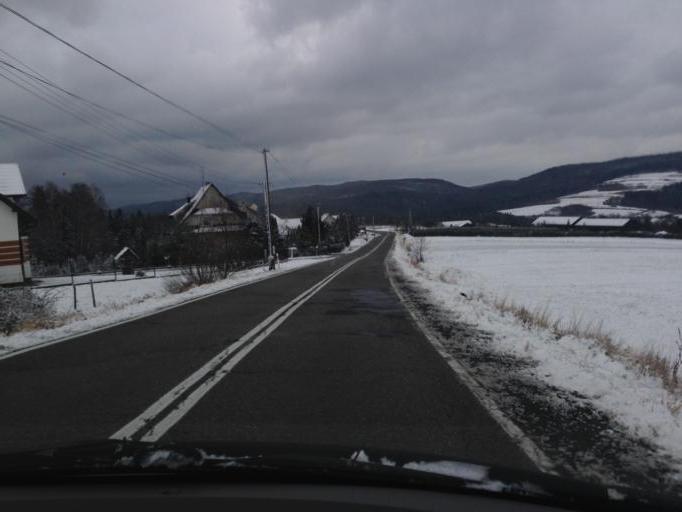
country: PL
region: Lesser Poland Voivodeship
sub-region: Powiat bochenski
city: Nowy Wisnicz
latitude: 49.8521
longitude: 20.4848
